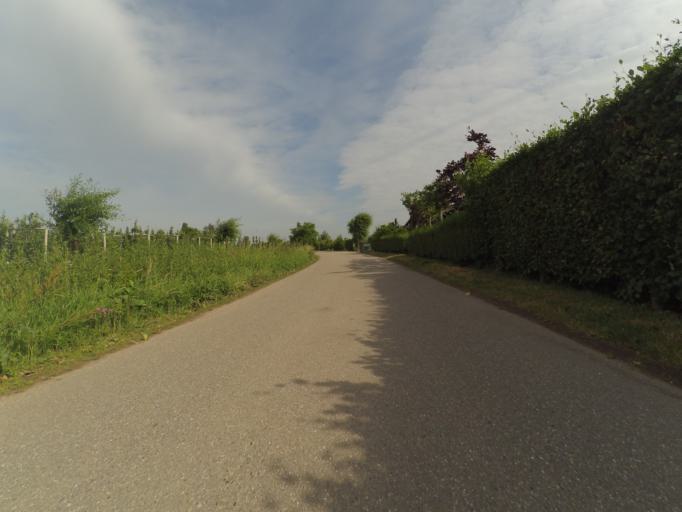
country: NL
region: Utrecht
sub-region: Gemeente Wijk bij Duurstede
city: Wijk bij Duurstede
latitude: 51.9447
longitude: 5.3448
